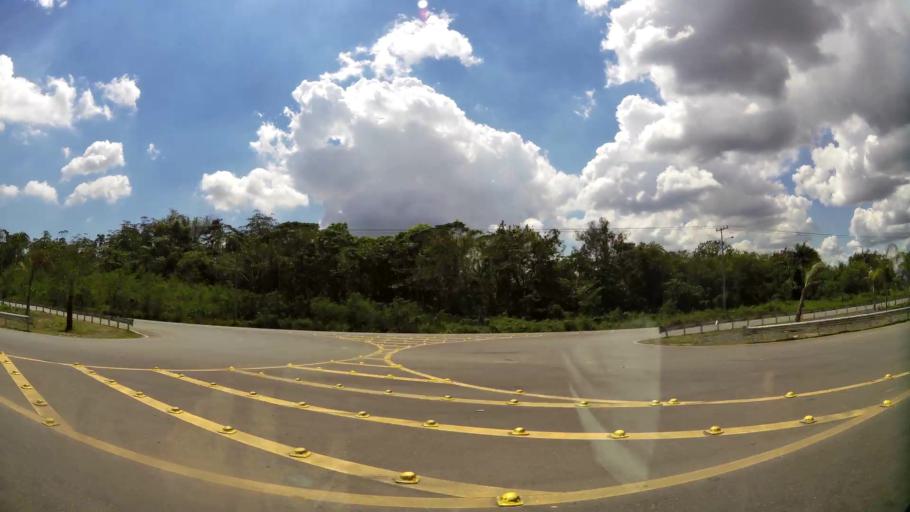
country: DO
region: Nacional
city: Santo Domingo
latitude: 18.5475
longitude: -69.9656
